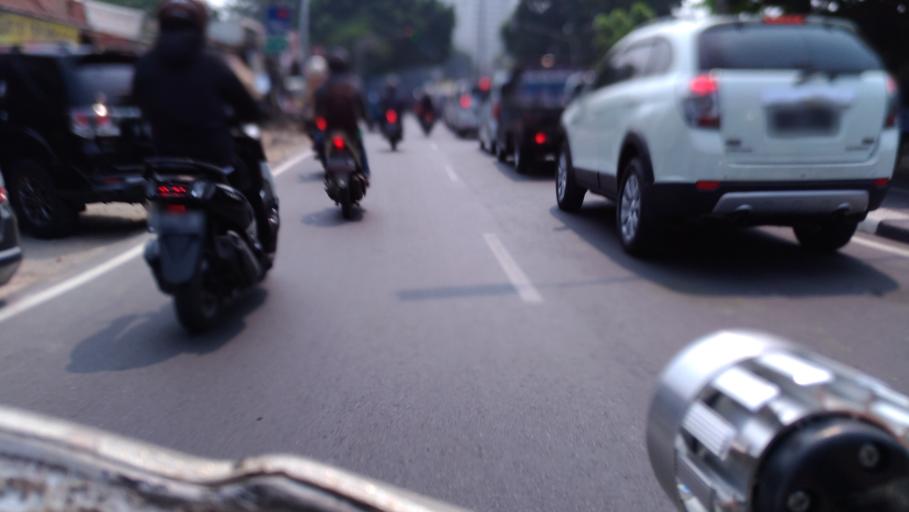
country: ID
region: West Java
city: Depok
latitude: -6.3441
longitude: 106.8685
